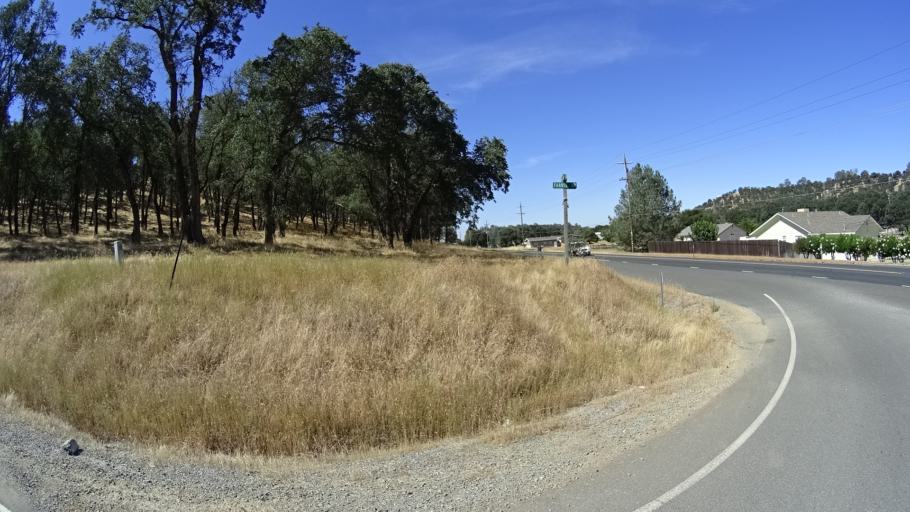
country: US
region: California
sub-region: Calaveras County
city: Rancho Calaveras
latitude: 38.1500
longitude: -120.8581
